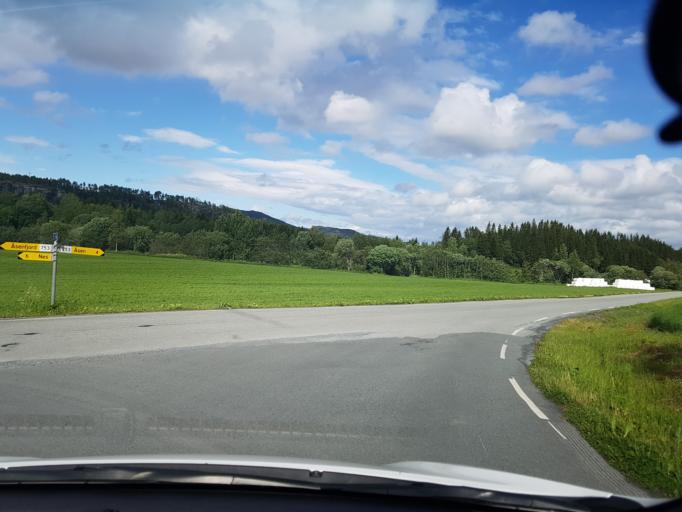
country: NO
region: Nord-Trondelag
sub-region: Stjordal
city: Stjordalshalsen
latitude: 63.5959
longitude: 10.9787
